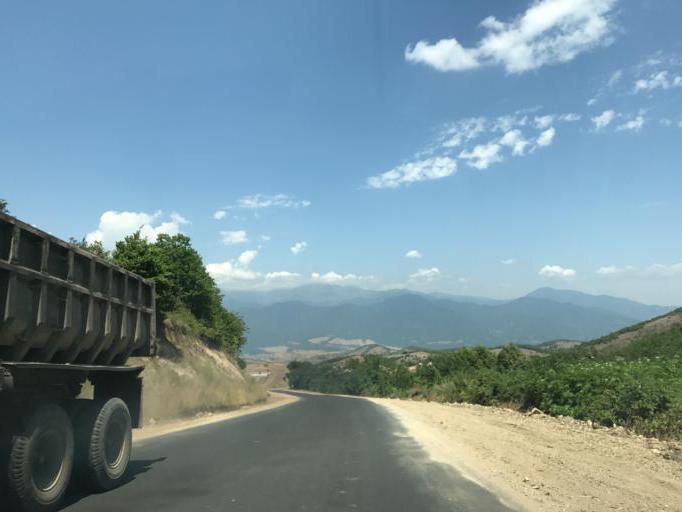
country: AZ
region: Tartar Rayon
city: Martakert
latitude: 40.1255
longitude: 46.6258
